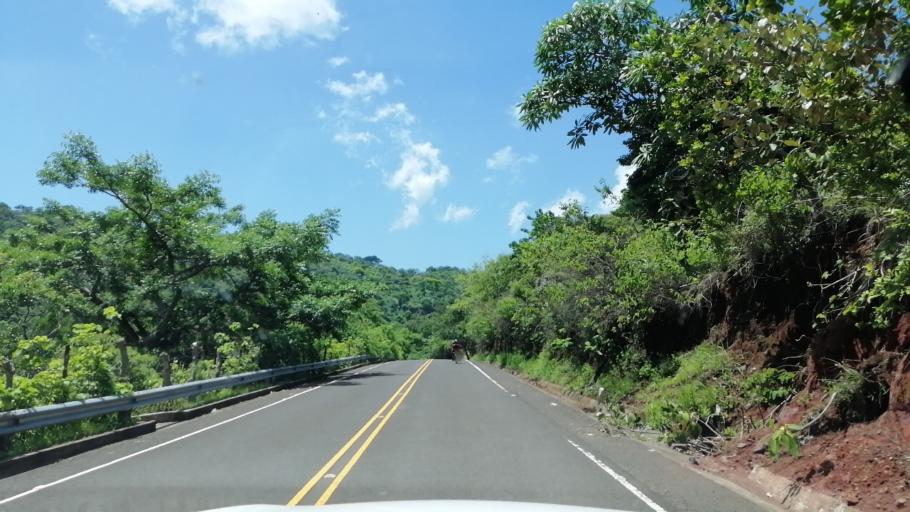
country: SV
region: San Miguel
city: Ciudad Barrios
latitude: 13.7971
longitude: -88.2950
